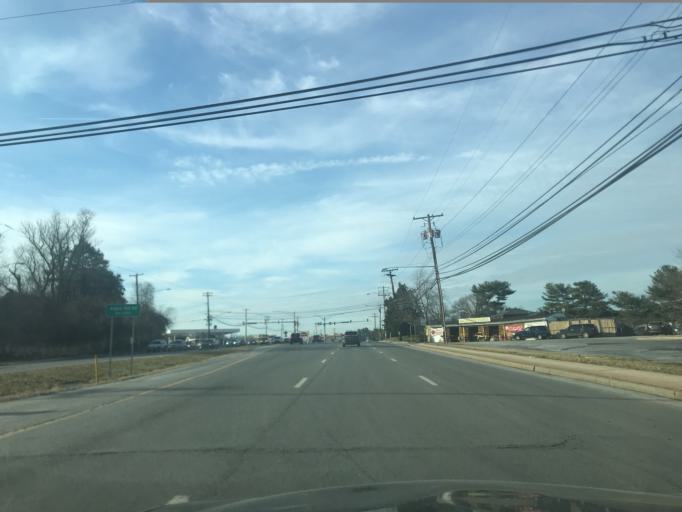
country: US
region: Maryland
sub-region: Montgomery County
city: Aspen Hill
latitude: 39.0796
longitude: -77.0734
